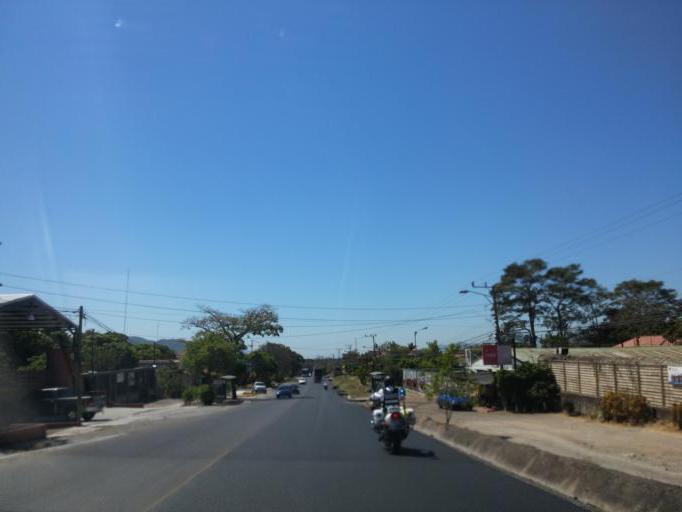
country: CR
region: Heredia
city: Colon
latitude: 9.9345
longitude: -84.2245
